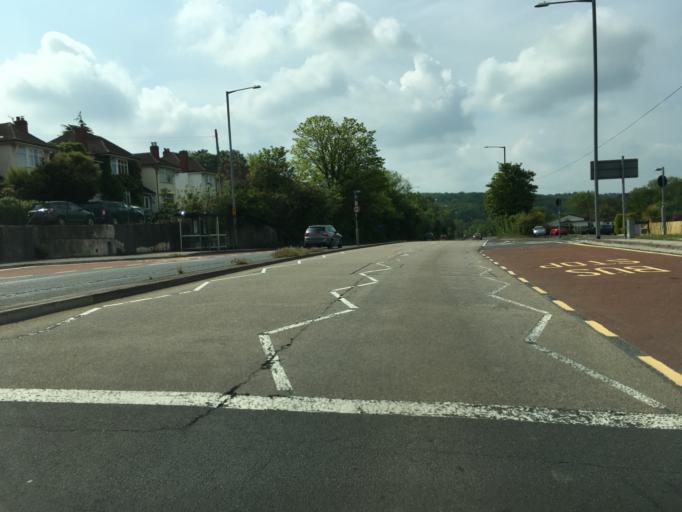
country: GB
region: England
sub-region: North Somerset
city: Long Ashton
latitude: 51.4790
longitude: -2.6479
